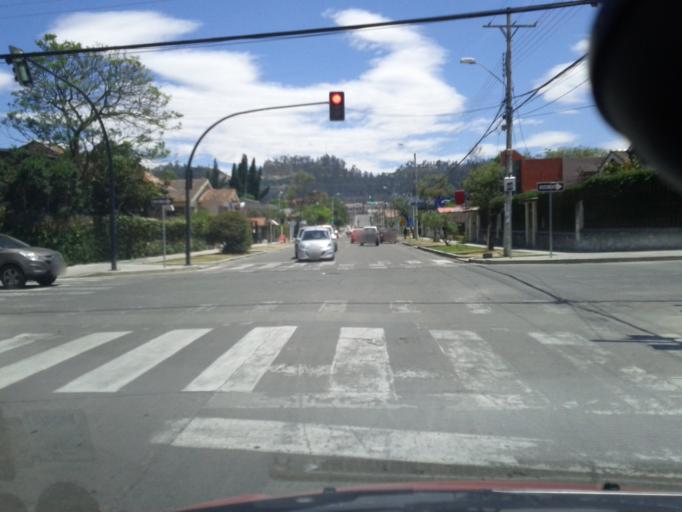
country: EC
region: Azuay
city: Cuenca
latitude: -2.9052
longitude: -79.0089
